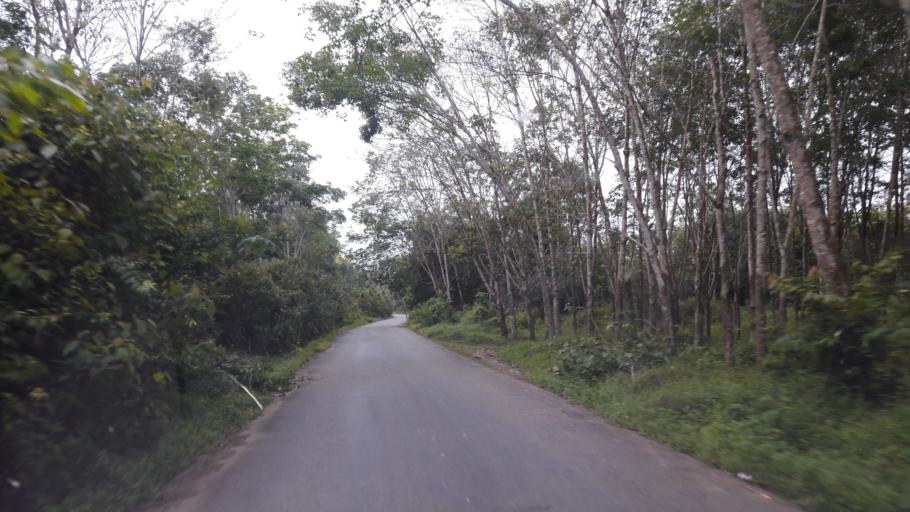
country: ID
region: South Sumatra
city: Gunungmenang
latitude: -3.1215
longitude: 104.1162
